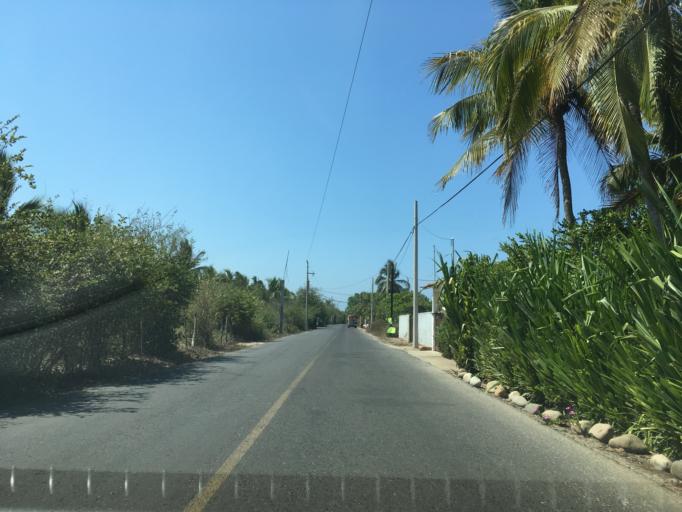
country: MX
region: Guerrero
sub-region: Zihuatanejo de Azueta
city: Los Achotes
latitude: 17.5483
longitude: -101.4385
